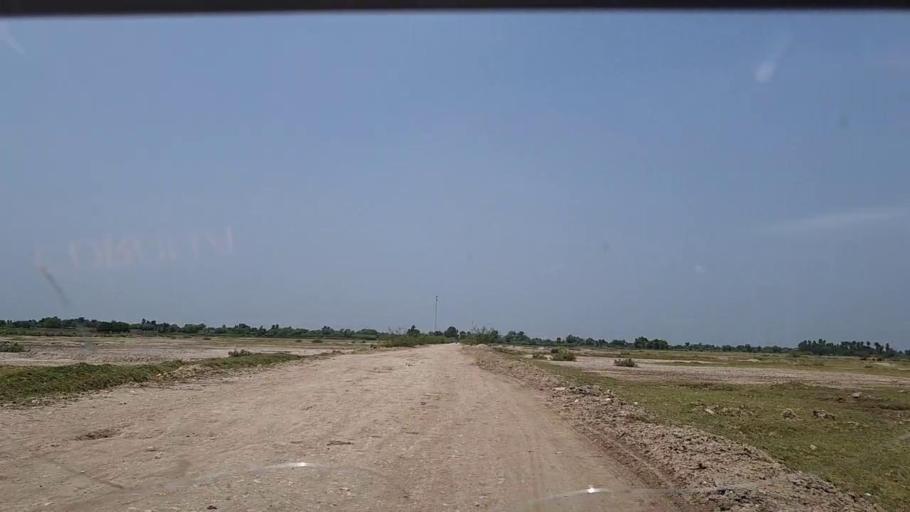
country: PK
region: Sindh
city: Adilpur
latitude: 27.9128
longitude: 69.2123
